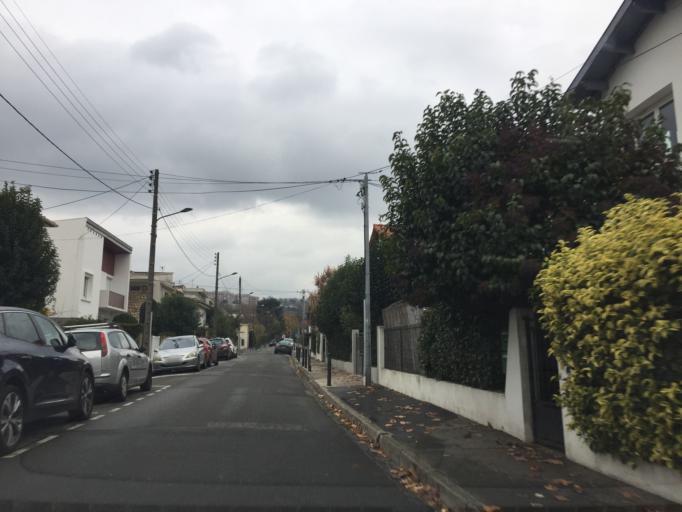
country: FR
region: Midi-Pyrenees
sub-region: Departement de la Haute-Garonne
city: Ramonville-Saint-Agne
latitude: 43.5689
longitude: 1.4606
